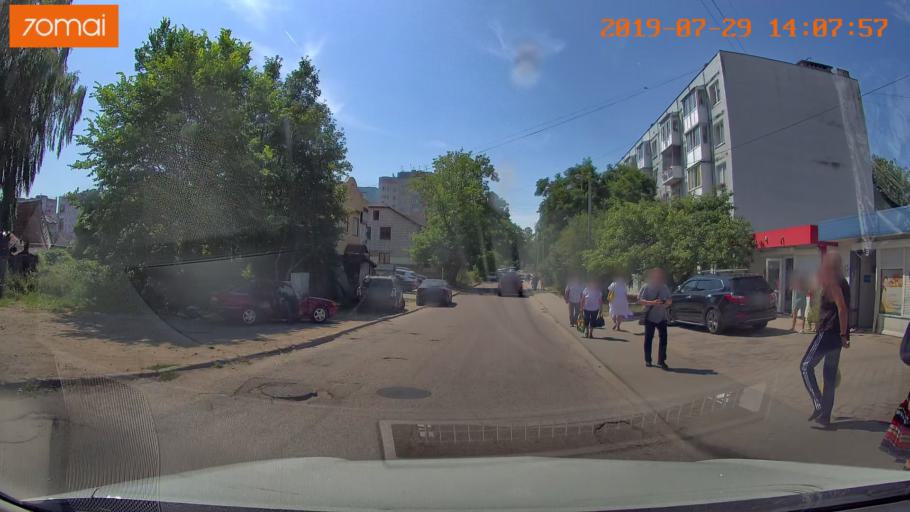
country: RU
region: Kaliningrad
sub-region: Gorod Kaliningrad
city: Baltiysk
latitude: 54.6578
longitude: 19.9088
